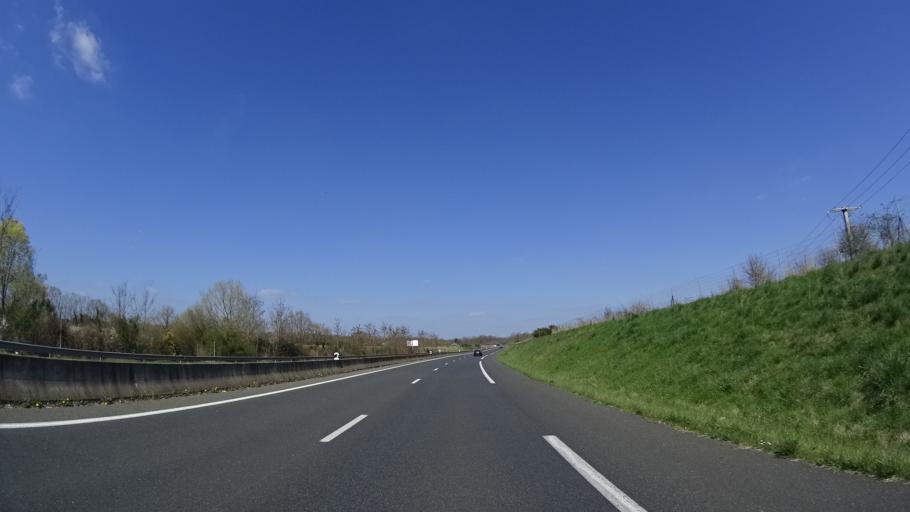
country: FR
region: Pays de la Loire
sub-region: Departement de Maine-et-Loire
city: Saint-Jean
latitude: 47.2960
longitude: -0.3894
